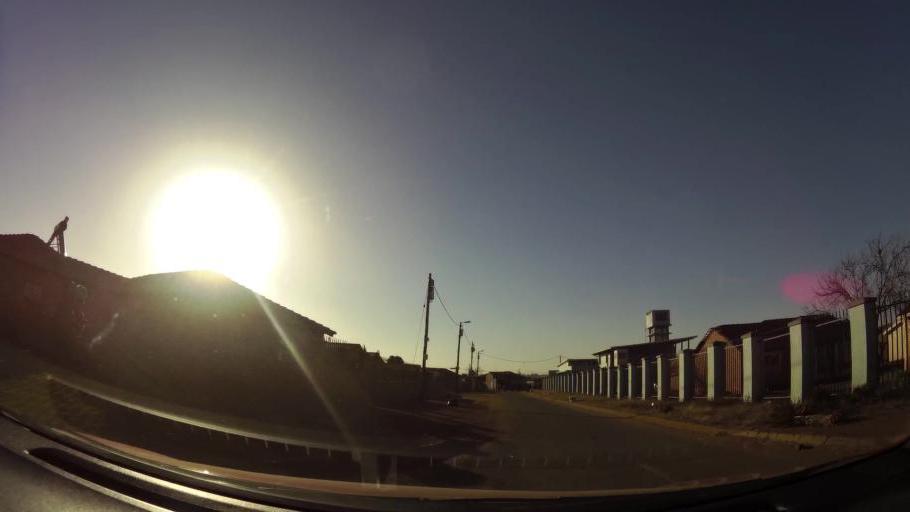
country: ZA
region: Gauteng
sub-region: City of Tshwane Metropolitan Municipality
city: Mabopane
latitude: -25.5960
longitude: 28.1057
